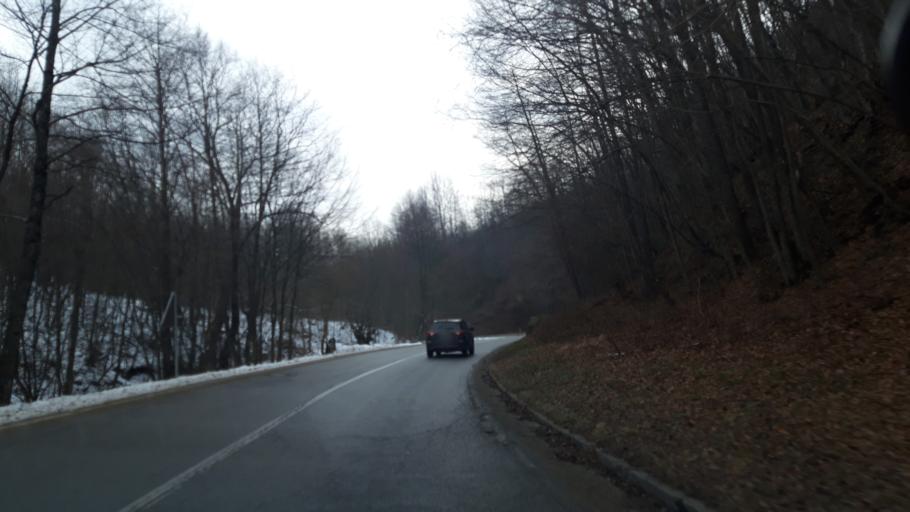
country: BA
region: Republika Srpska
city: Vlasenica
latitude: 44.1820
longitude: 19.0080
